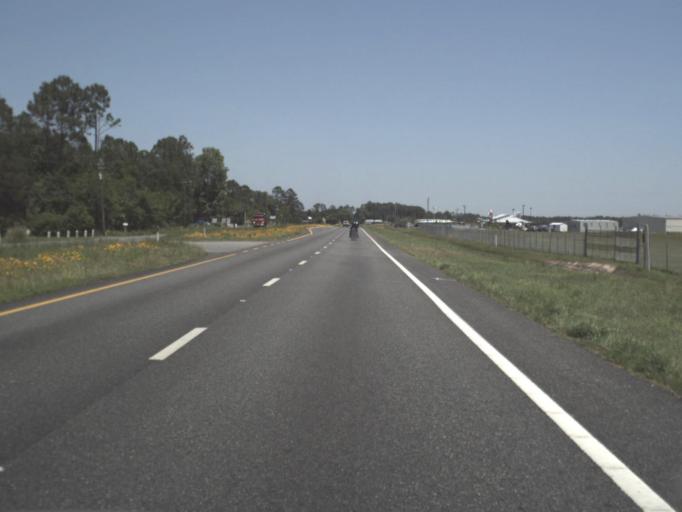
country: US
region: Florida
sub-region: Columbia County
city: Watertown
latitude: 30.1868
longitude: -82.5864
